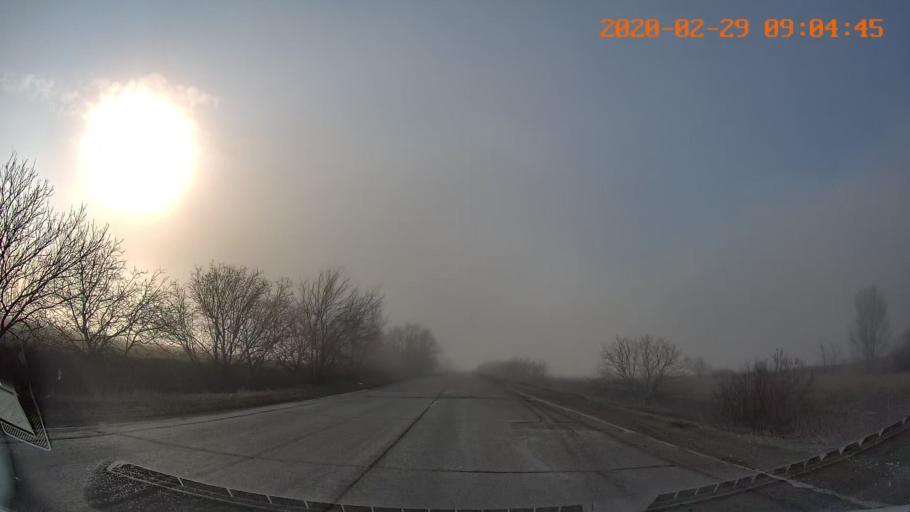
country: MD
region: Telenesti
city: Tiraspolul Nou
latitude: 46.8980
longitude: 29.7375
